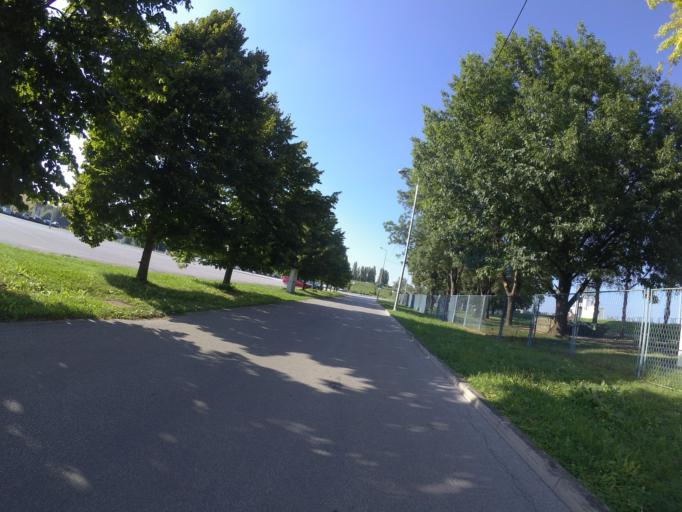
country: HR
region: Karlovacka
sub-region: Grad Karlovac
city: Karlovac
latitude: 45.4838
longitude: 15.5628
